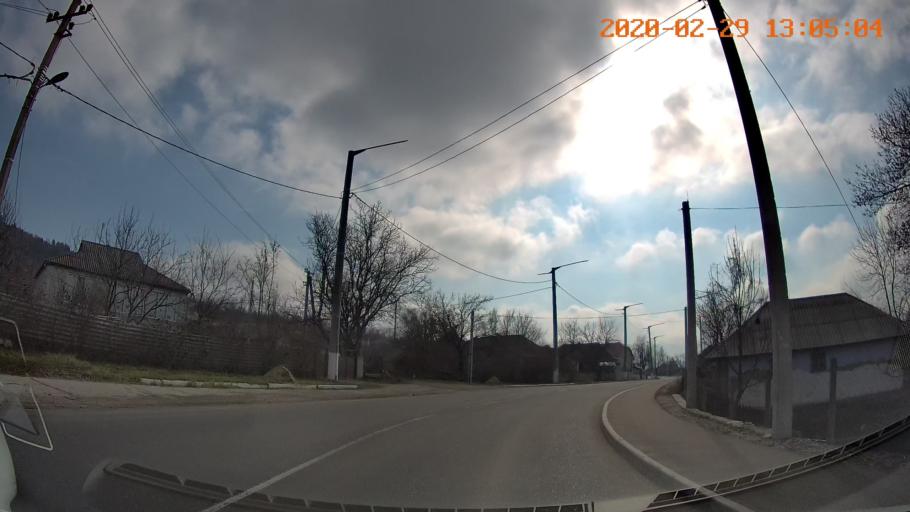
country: MD
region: Telenesti
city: Camenca
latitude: 48.0231
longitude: 28.7083
